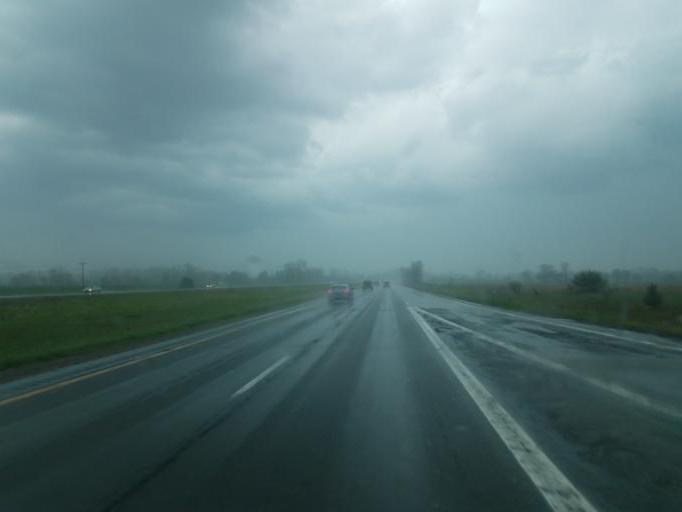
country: US
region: Michigan
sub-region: Livingston County
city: Fowlerville
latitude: 42.6505
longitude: -84.1243
